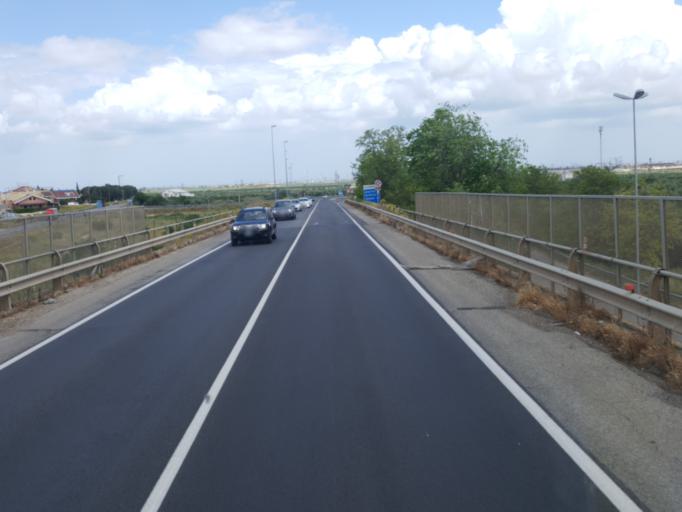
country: IT
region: Apulia
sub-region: Provincia di Bari
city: Palo del Colle
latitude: 41.0539
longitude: 16.7107
